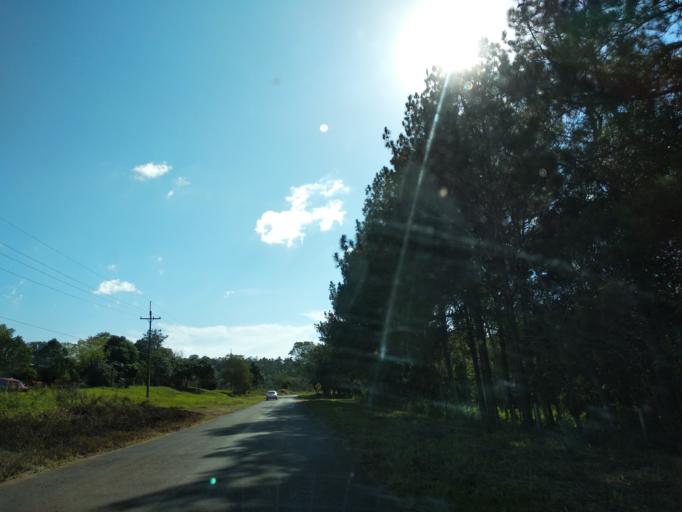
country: PY
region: Itapua
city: Hohenau
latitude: -27.0957
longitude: -55.7008
